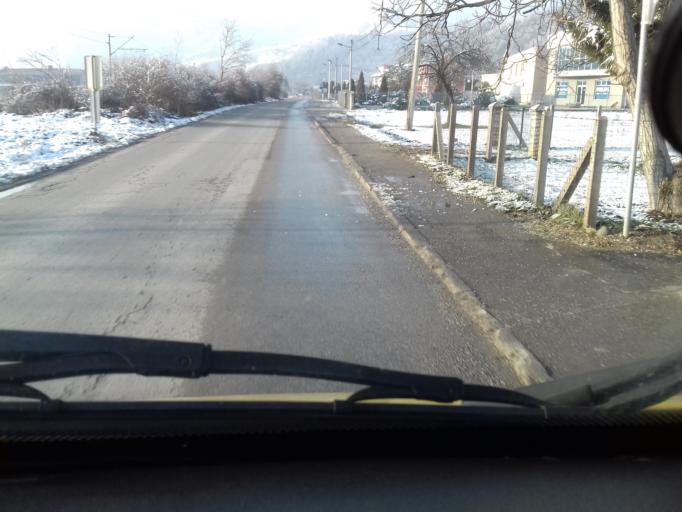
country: BA
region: Federation of Bosnia and Herzegovina
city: Mahala
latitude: 43.9932
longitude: 18.2240
